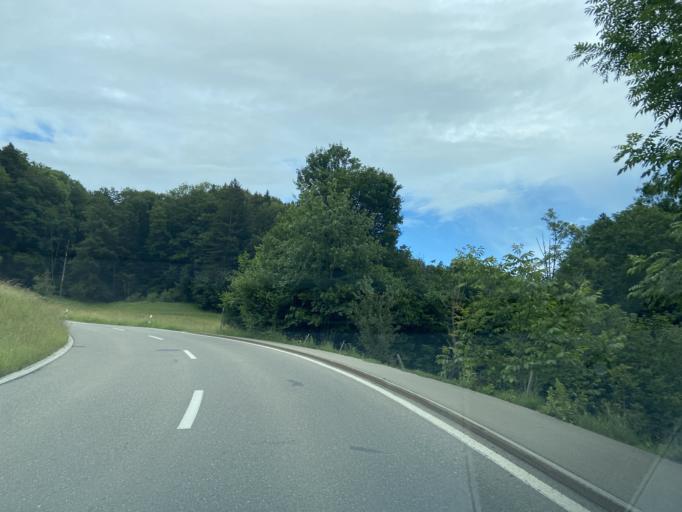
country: CH
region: Thurgau
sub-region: Muenchwilen District
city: Aadorf
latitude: 47.4601
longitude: 8.8959
